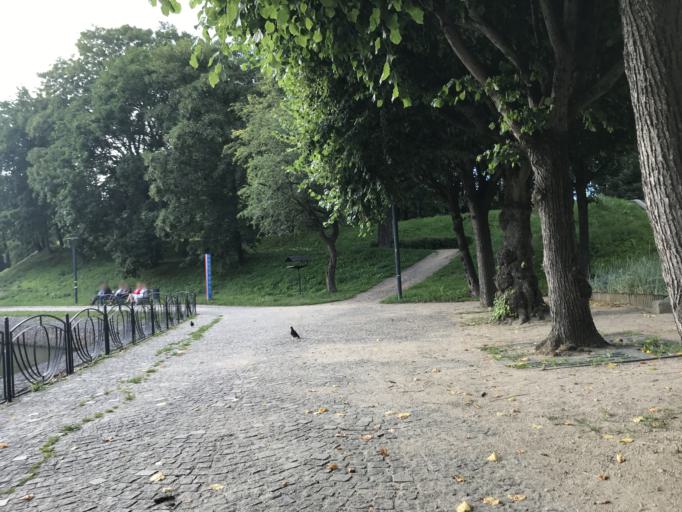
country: PL
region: Pomeranian Voivodeship
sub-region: Gdansk
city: Gdansk
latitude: 54.3519
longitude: 18.6375
